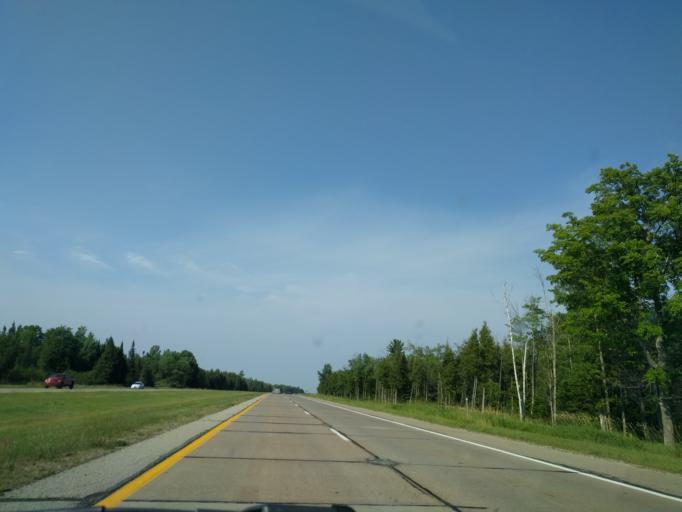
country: US
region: Michigan
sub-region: Delta County
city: Gladstone
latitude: 45.8839
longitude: -87.0098
